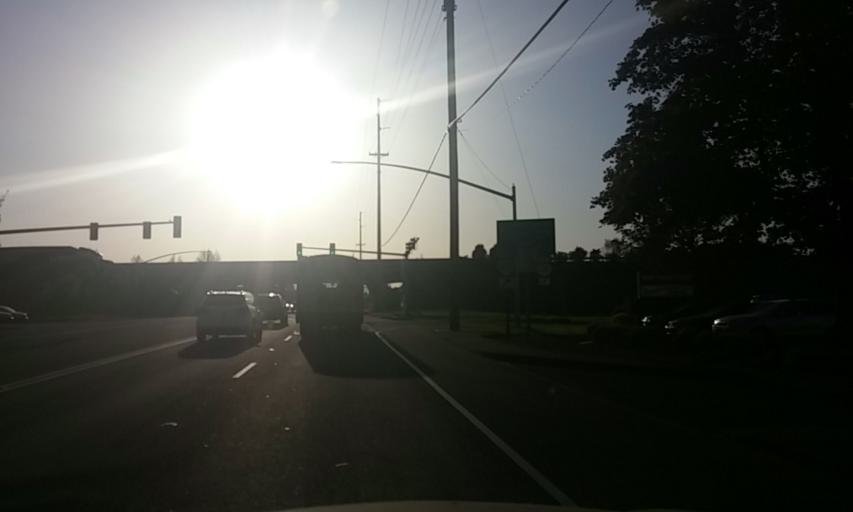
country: US
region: Oregon
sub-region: Washington County
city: Beaverton
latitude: 45.4864
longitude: -122.7946
